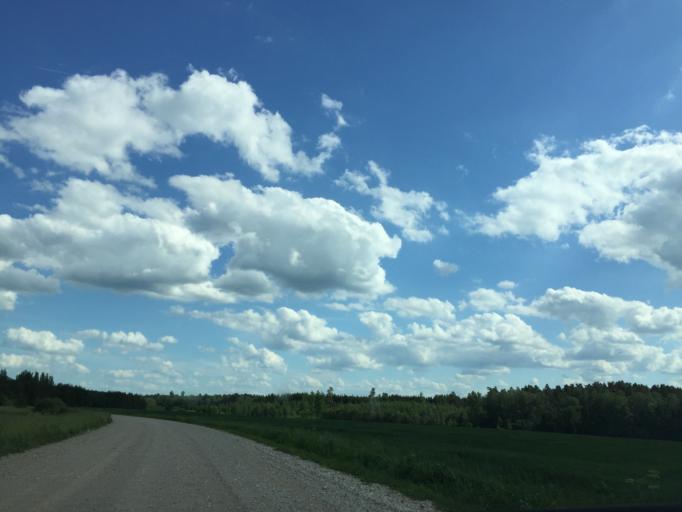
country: LV
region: Jaunpils
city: Jaunpils
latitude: 56.8140
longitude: 23.0727
